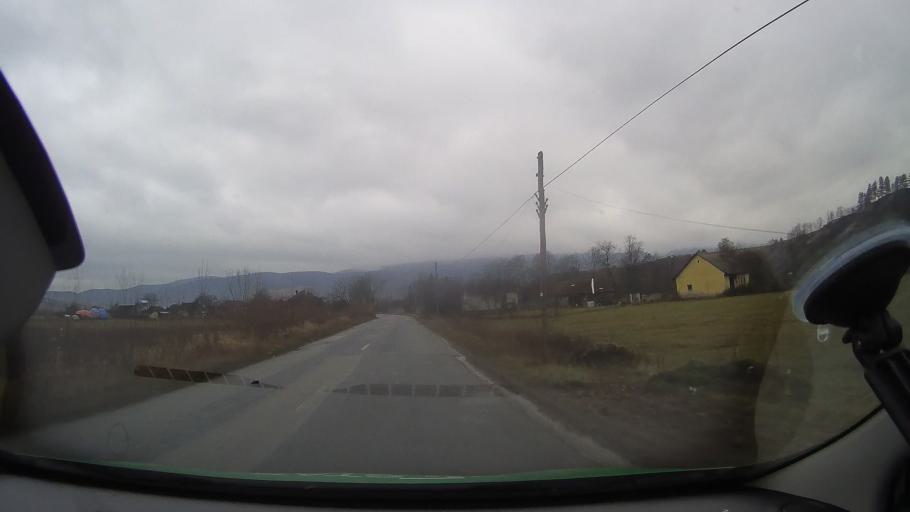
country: RO
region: Arad
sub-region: Comuna Halmagiu
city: Halmagiu
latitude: 46.2600
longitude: 22.5797
